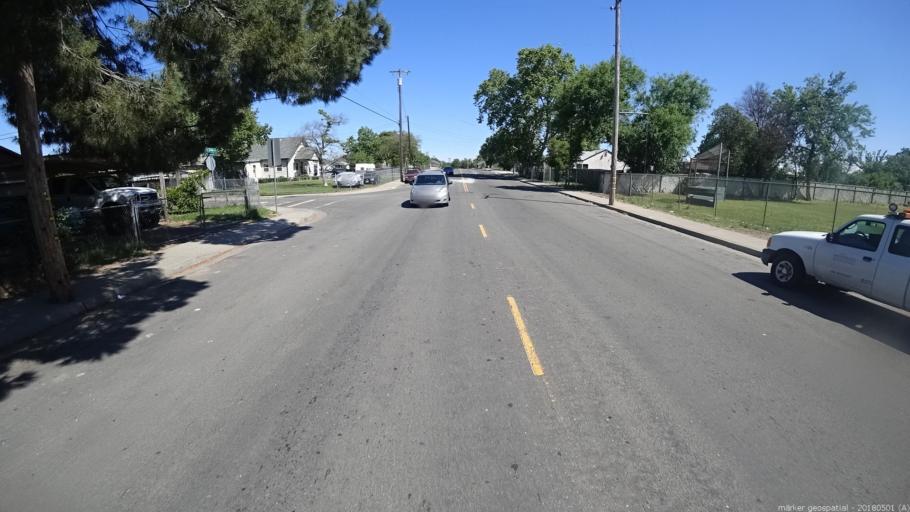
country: US
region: California
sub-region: Sacramento County
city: Rio Linda
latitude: 38.6414
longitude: -121.4385
